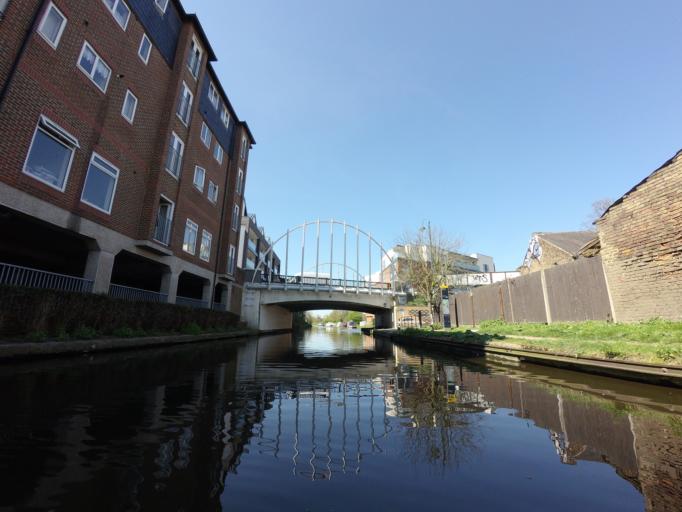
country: GB
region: England
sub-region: Greater London
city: West Drayton
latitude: 51.5108
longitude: -0.4728
